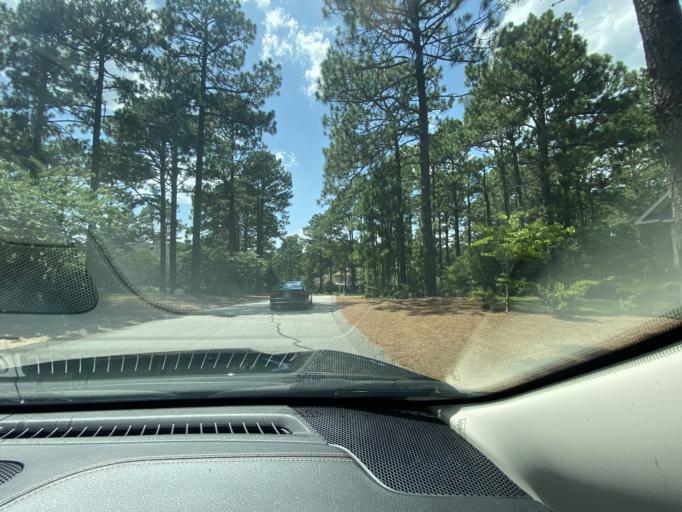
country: US
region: North Carolina
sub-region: Moore County
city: Pinehurst
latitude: 35.1951
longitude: -79.4293
